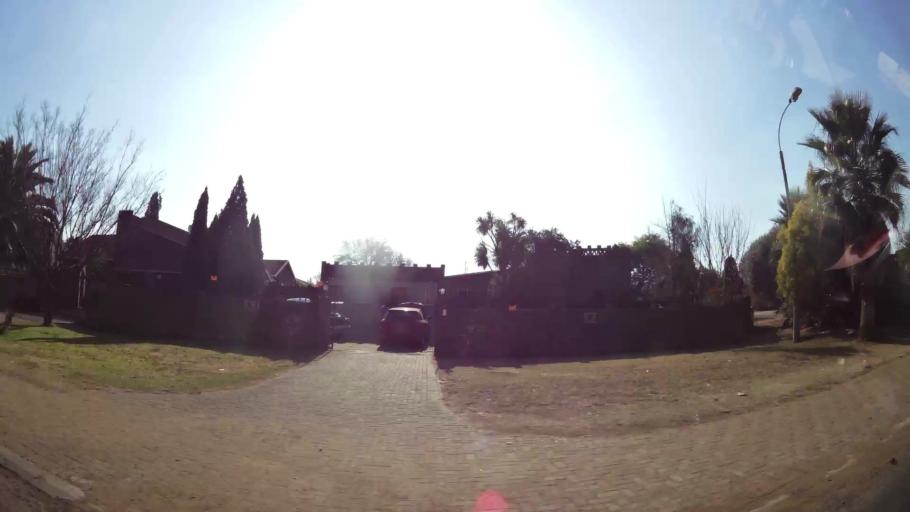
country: ZA
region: Gauteng
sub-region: West Rand District Municipality
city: Randfontein
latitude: -26.1845
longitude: 27.6841
